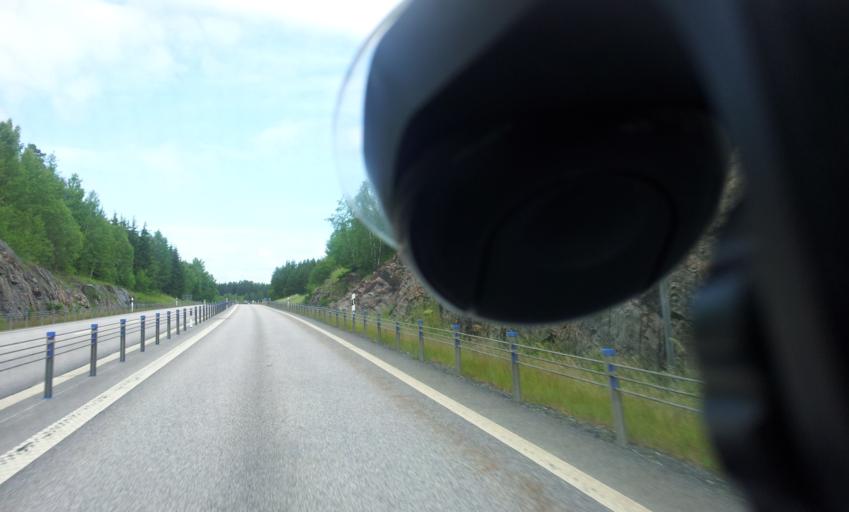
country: SE
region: OEstergoetland
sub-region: Valdemarsviks Kommun
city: Valdemarsvik
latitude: 58.2152
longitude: 16.5569
